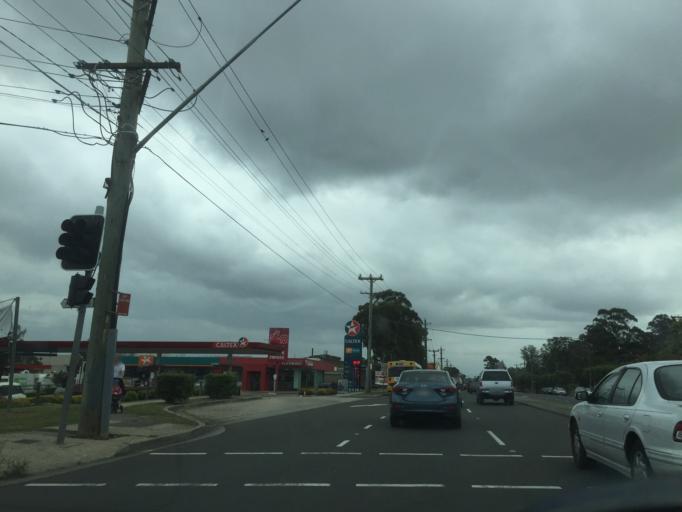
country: AU
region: New South Wales
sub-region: Parramatta
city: Northmead
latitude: -33.7663
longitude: 150.9556
